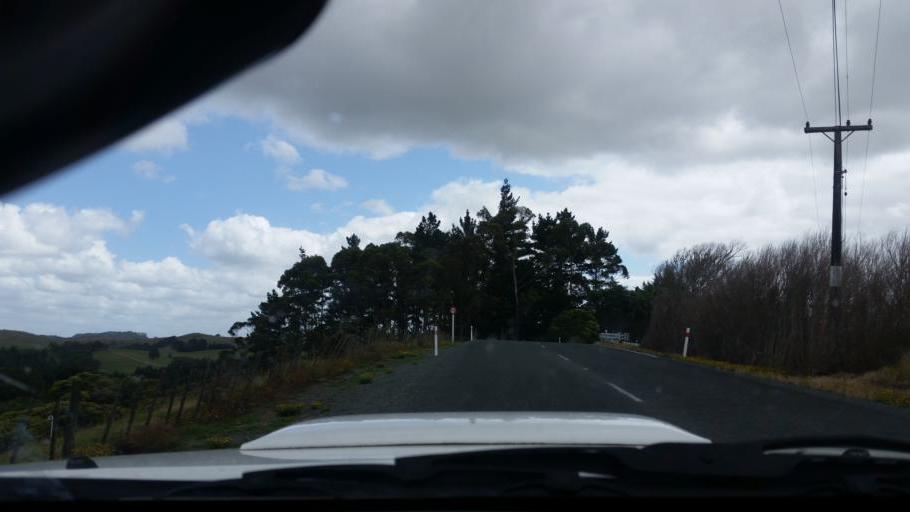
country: NZ
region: Northland
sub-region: Whangarei
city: Ruakaka
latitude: -36.1043
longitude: 174.3503
